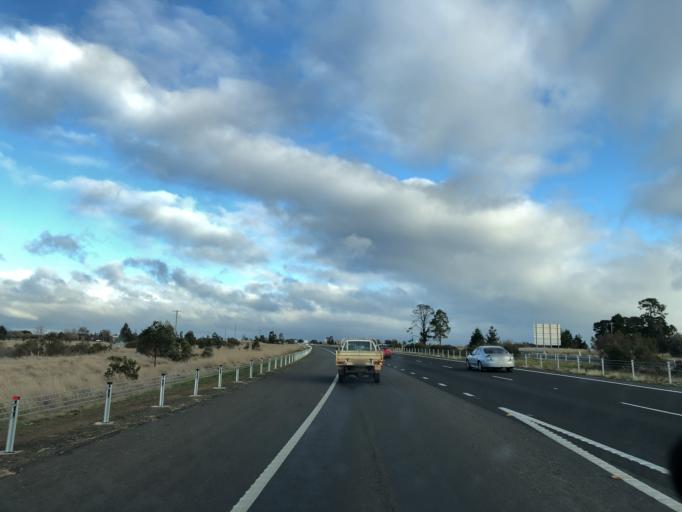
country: AU
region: Victoria
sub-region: Mount Alexander
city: Castlemaine
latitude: -37.1952
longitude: 144.4054
